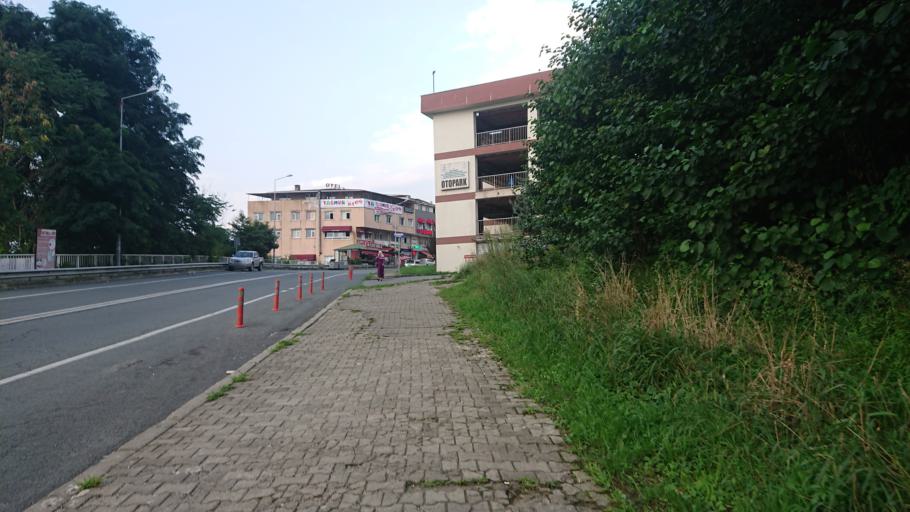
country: TR
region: Rize
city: Gundogdu
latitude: 41.0386
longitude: 40.5714
